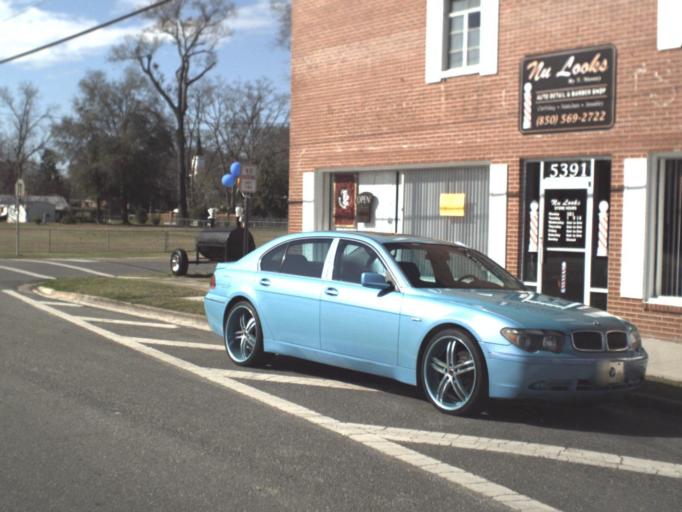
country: US
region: Florida
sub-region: Jackson County
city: Malone
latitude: 30.9565
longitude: -85.1624
